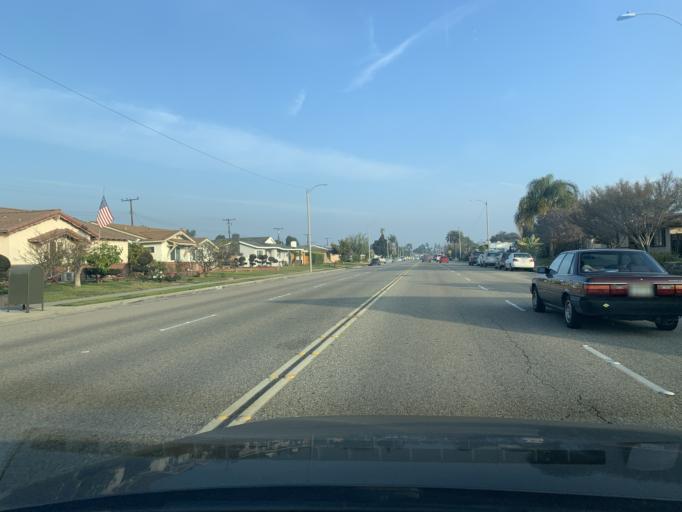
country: US
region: California
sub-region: Orange County
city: Westminster
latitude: 33.7657
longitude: -118.0256
